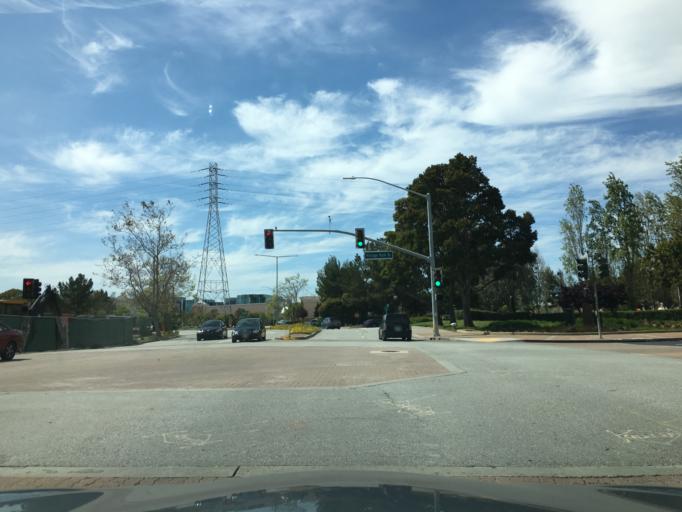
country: US
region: California
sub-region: San Mateo County
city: Foster City
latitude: 37.5624
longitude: -122.2781
